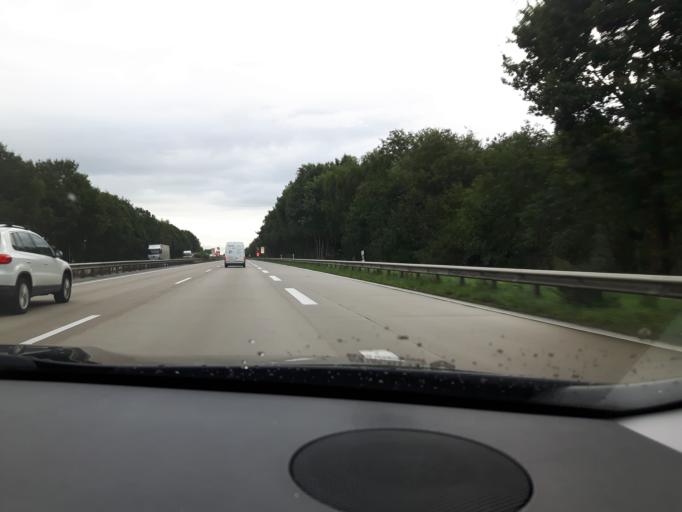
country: DE
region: Lower Saxony
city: Gross Ippener
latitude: 52.9750
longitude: 8.6214
